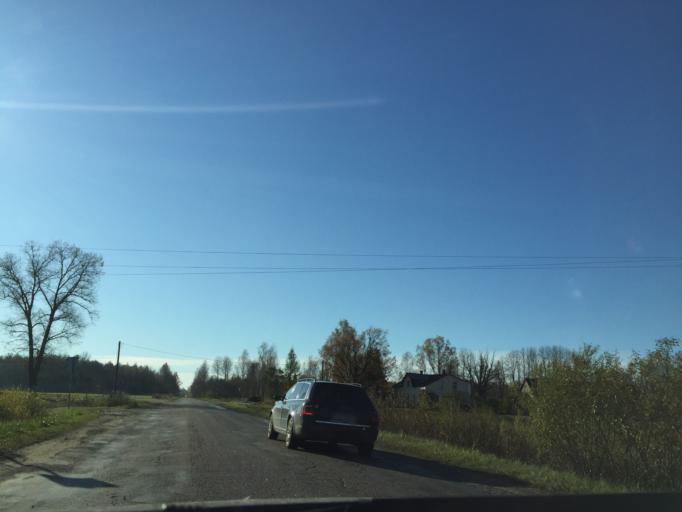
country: LV
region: Skriveri
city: Skriveri
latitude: 56.7235
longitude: 25.1597
